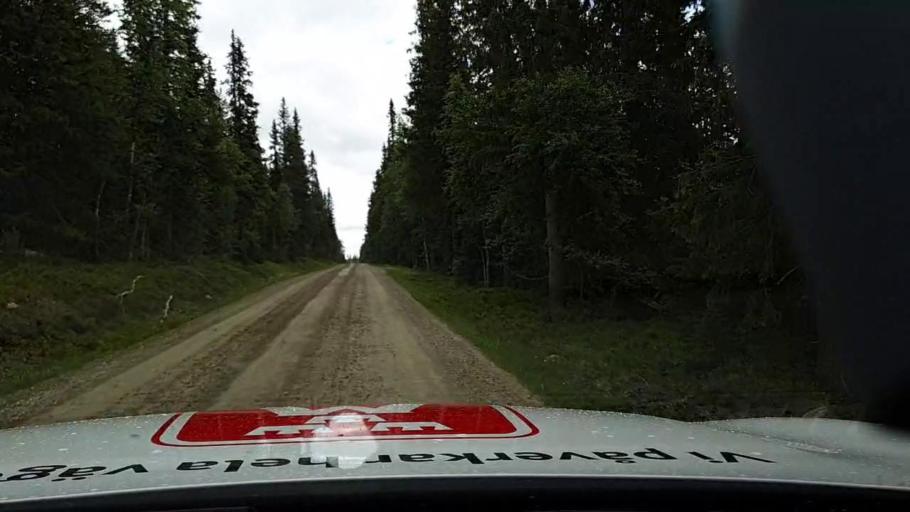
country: SE
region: Jaemtland
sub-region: Are Kommun
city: Jarpen
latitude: 62.6030
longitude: 13.2261
